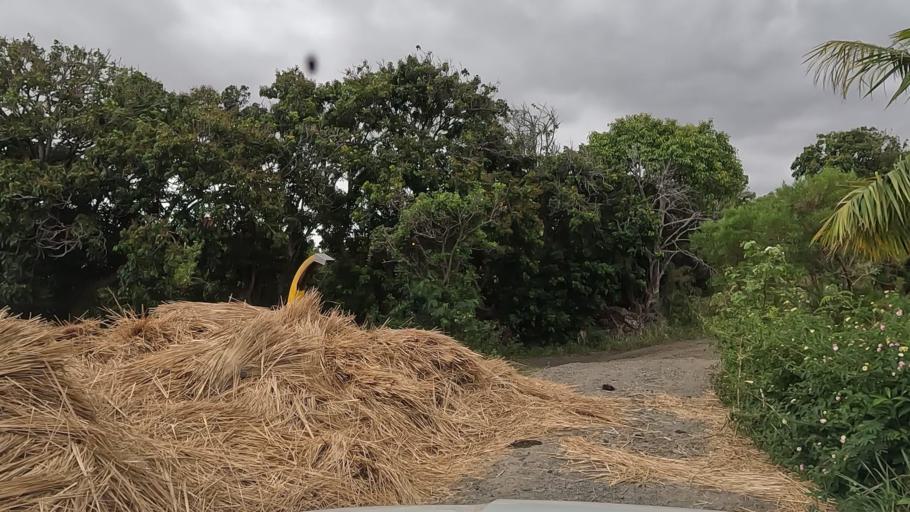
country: RE
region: Reunion
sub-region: Reunion
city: Saint-Pierre
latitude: -21.3389
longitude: 55.5221
